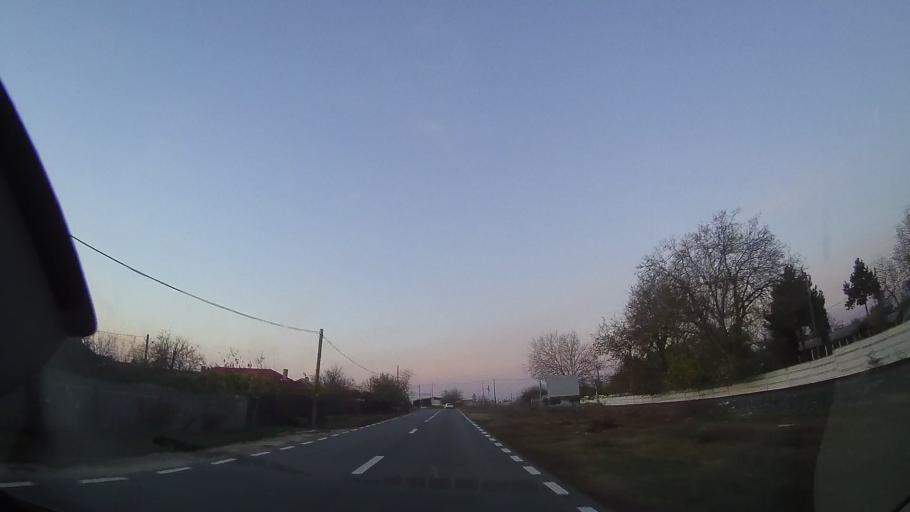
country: RO
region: Constanta
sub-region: Comuna Cobadin
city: Cobadin
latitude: 44.0540
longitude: 28.2466
